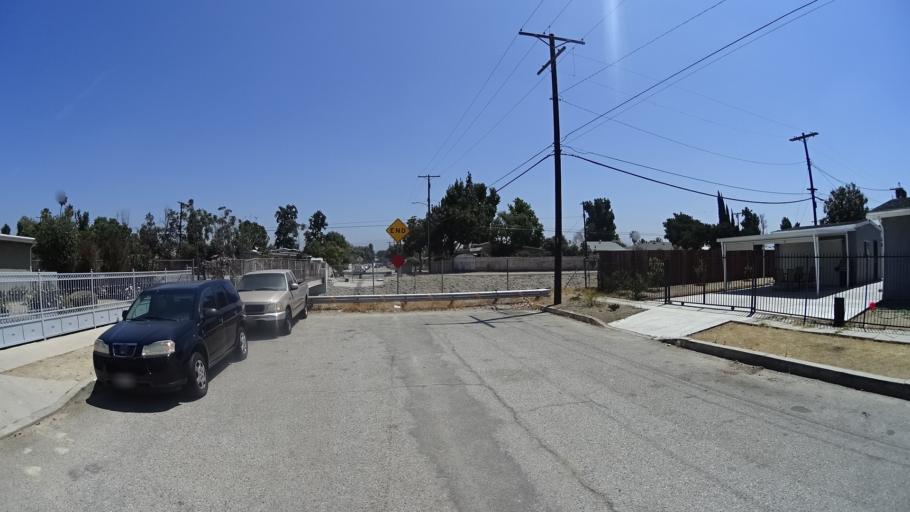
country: US
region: California
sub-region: Los Angeles County
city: San Fernando
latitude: 34.2378
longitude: -118.4247
